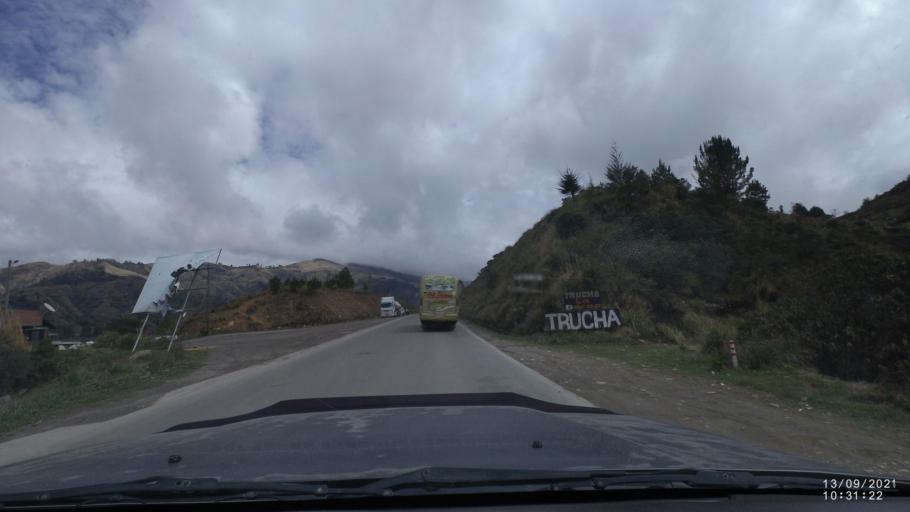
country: BO
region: Cochabamba
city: Colomi
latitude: -17.2546
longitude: -65.8926
